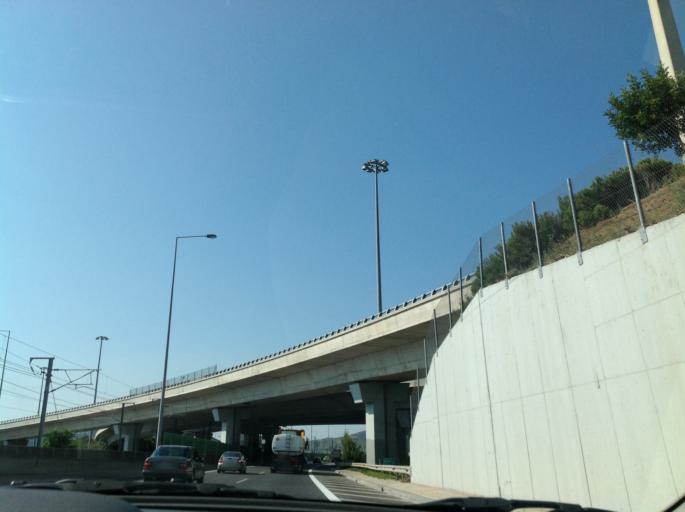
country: GR
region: Attica
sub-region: Nomarchia Anatolikis Attikis
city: Pallini
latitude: 37.9961
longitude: 23.8722
